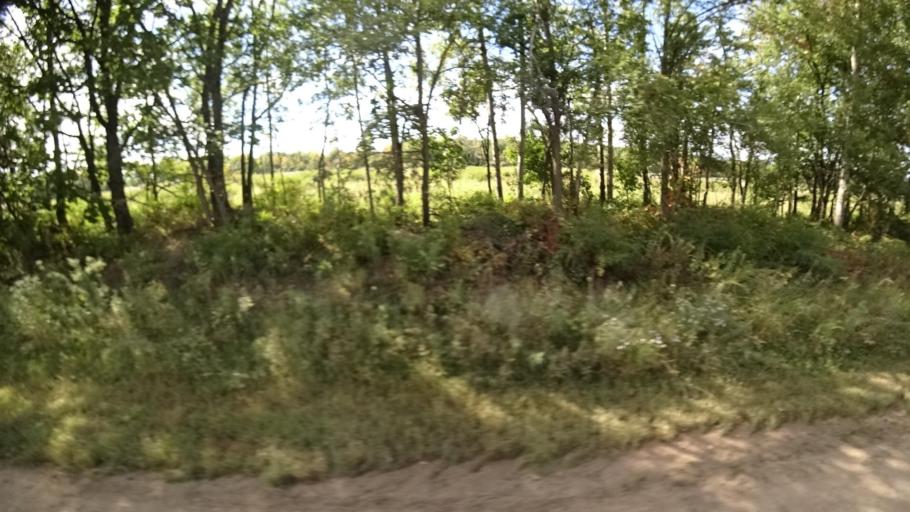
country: RU
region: Primorskiy
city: Yakovlevka
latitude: 44.4204
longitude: 133.5712
